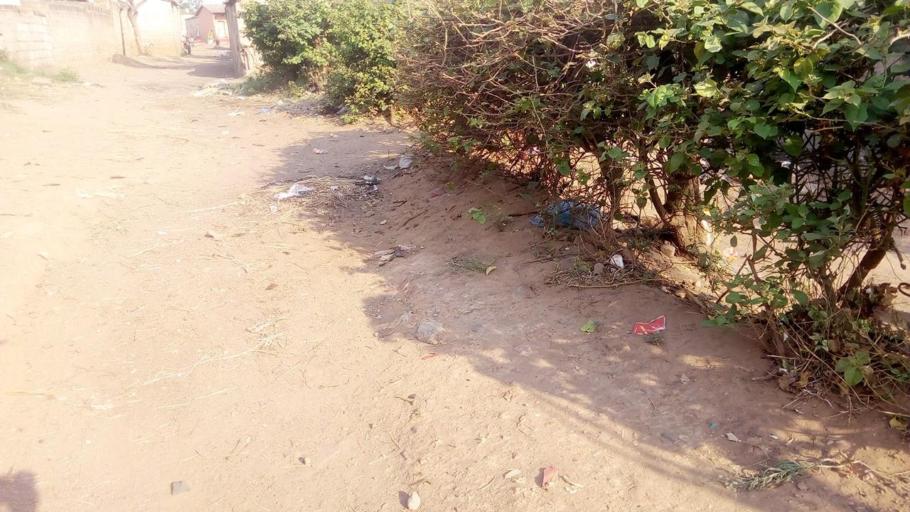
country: ZM
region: Lusaka
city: Lusaka
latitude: -15.3630
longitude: 28.3008
